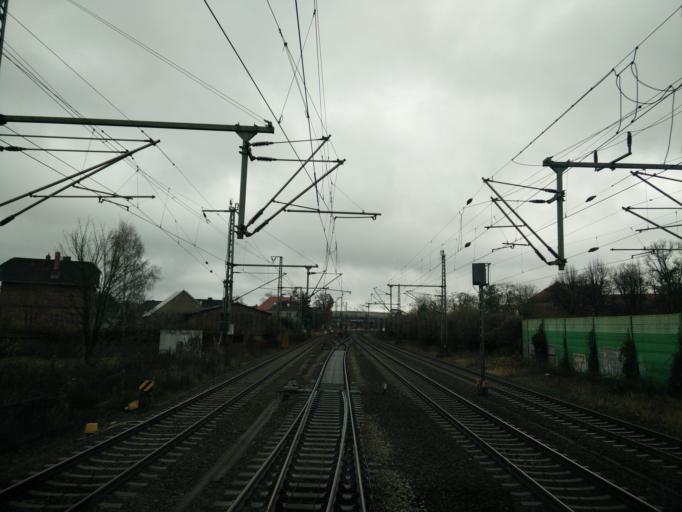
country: DE
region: Mecklenburg-Vorpommern
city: Ludwigslust
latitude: 53.3336
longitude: 11.4970
